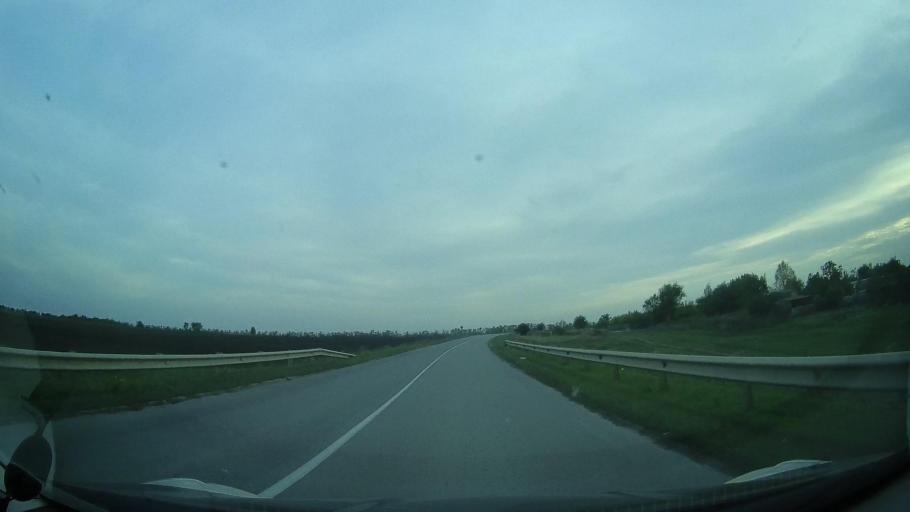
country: RU
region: Rostov
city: Kirovskaya
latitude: 47.0332
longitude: 39.9813
